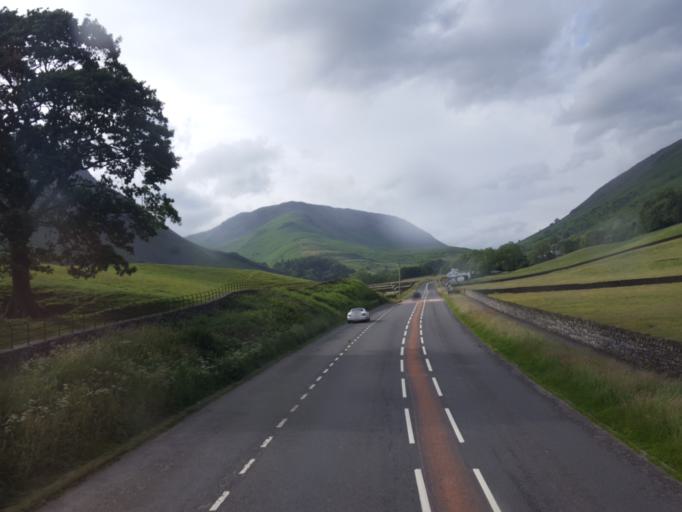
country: GB
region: England
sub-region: Cumbria
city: Ambleside
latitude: 54.4676
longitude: -3.0231
